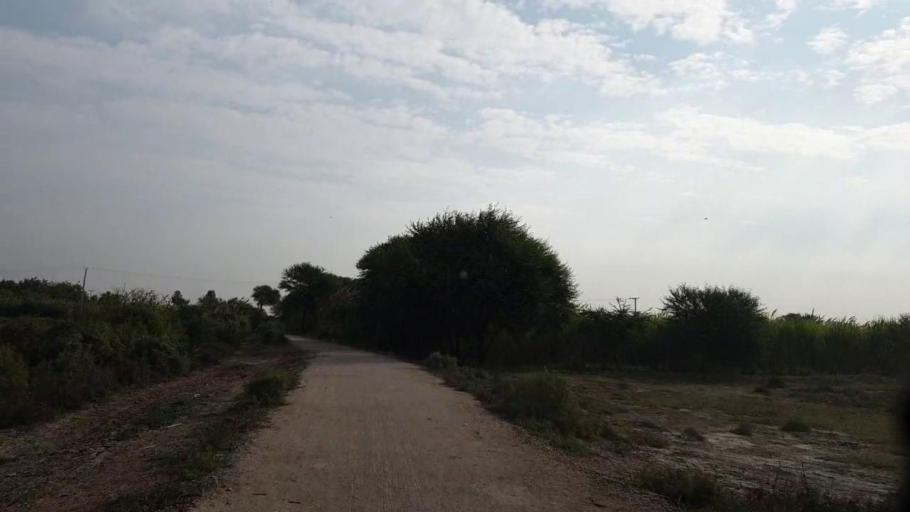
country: PK
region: Sindh
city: Tando Muhammad Khan
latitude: 25.0233
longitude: 68.4537
